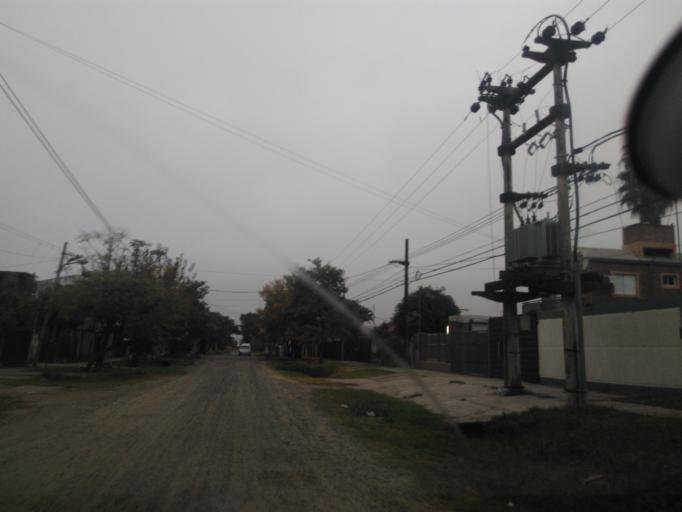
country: AR
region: Chaco
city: Resistencia
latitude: -27.4719
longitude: -58.9992
